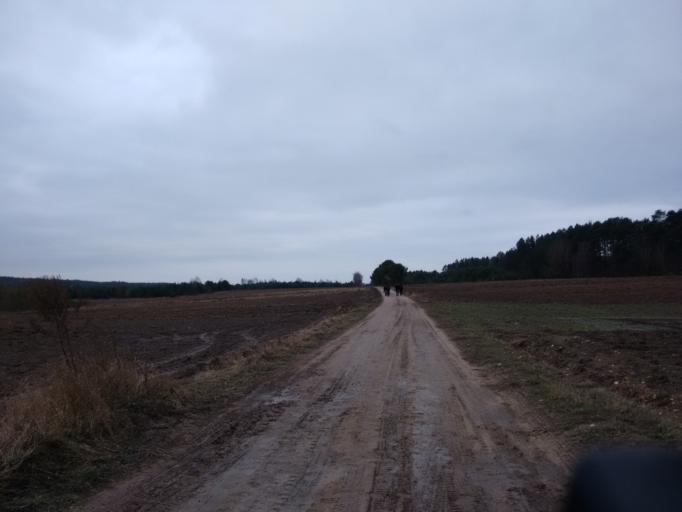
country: LT
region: Alytaus apskritis
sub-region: Alytus
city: Alytus
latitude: 54.2266
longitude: 23.9581
